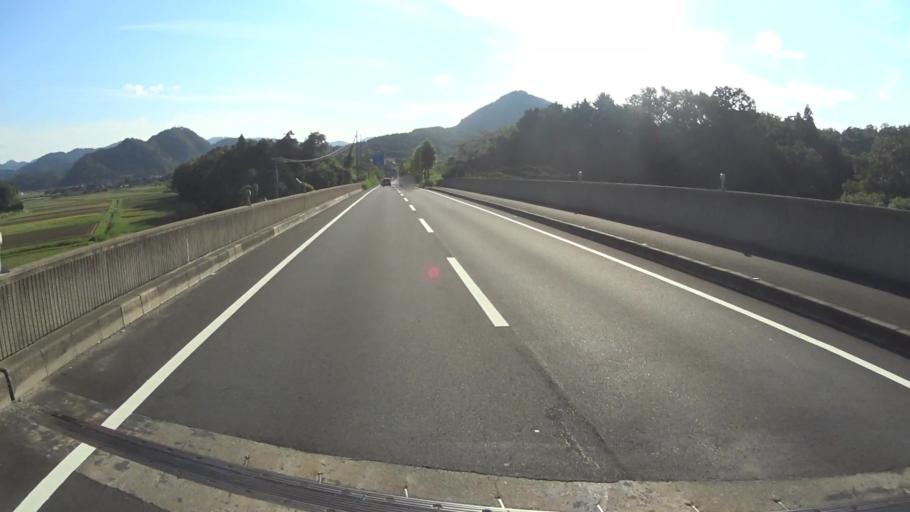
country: JP
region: Hyogo
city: Toyooka
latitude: 35.6194
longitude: 134.9253
